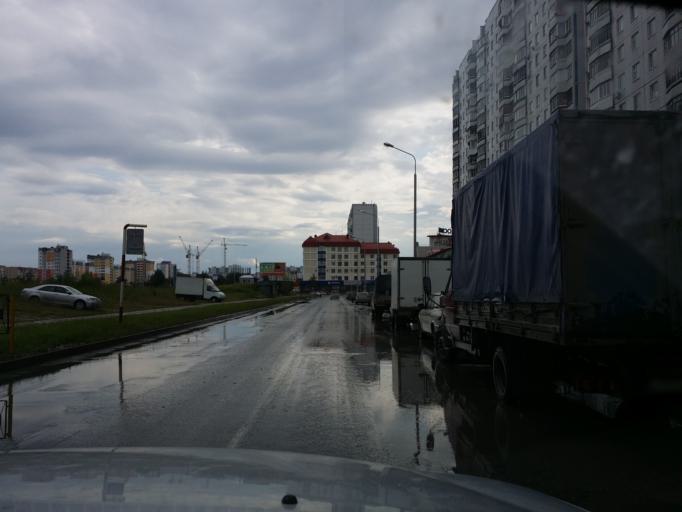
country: RU
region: Khanty-Mansiyskiy Avtonomnyy Okrug
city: Nizhnevartovsk
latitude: 60.9379
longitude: 76.5875
